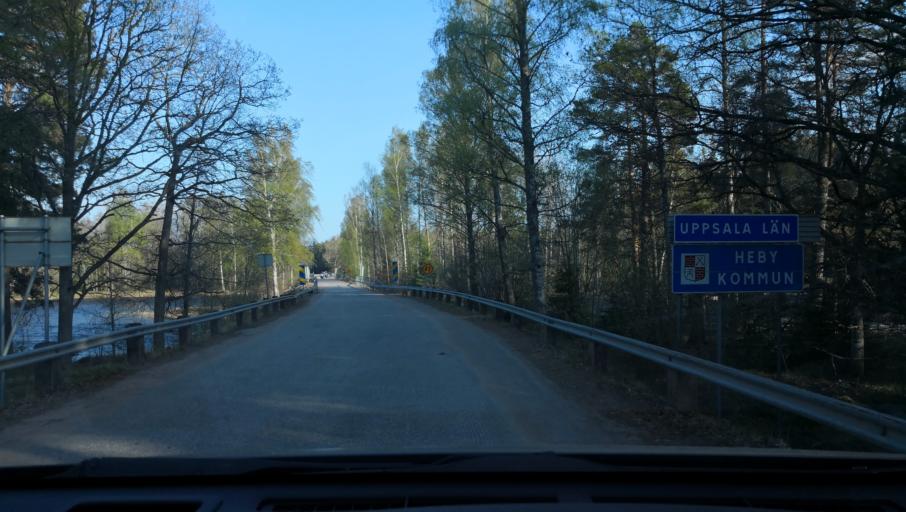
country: SE
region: Uppsala
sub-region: Heby Kommun
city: Tarnsjo
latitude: 60.2691
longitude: 16.9104
